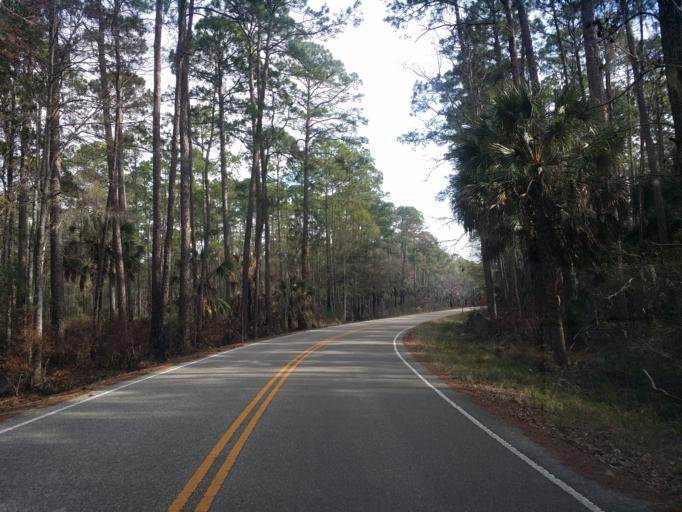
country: US
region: Florida
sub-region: Leon County
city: Woodville
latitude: 30.1517
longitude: -84.1453
